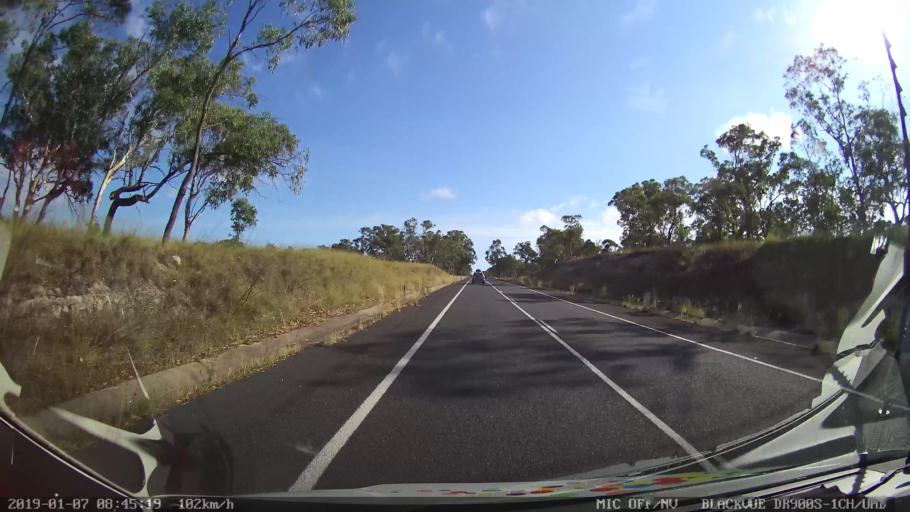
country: AU
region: New South Wales
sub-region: Tamworth Municipality
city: Kootingal
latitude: -30.8207
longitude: 151.2241
